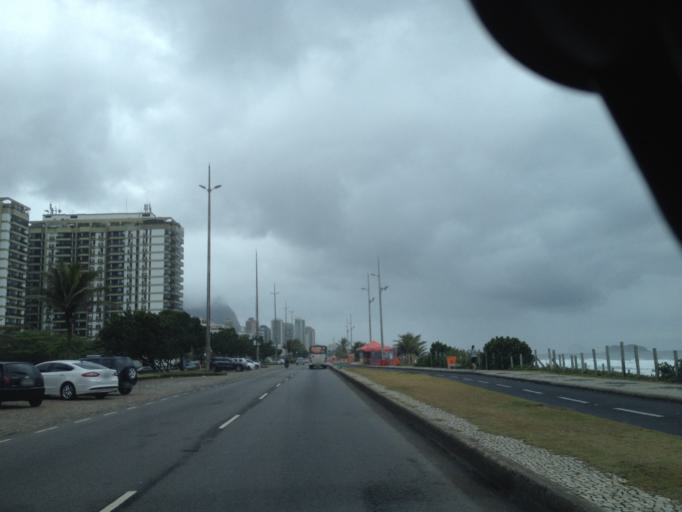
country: BR
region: Rio de Janeiro
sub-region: Rio De Janeiro
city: Rio de Janeiro
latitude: -23.0103
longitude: -43.3476
